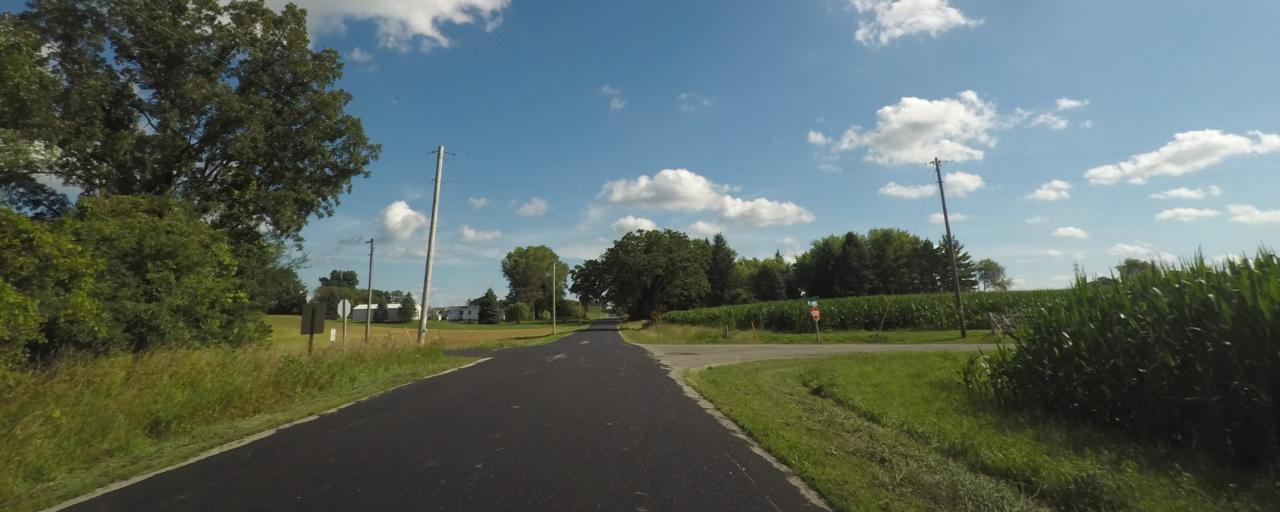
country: US
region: Wisconsin
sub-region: Rock County
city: Edgerton
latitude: 42.8692
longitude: -89.1321
